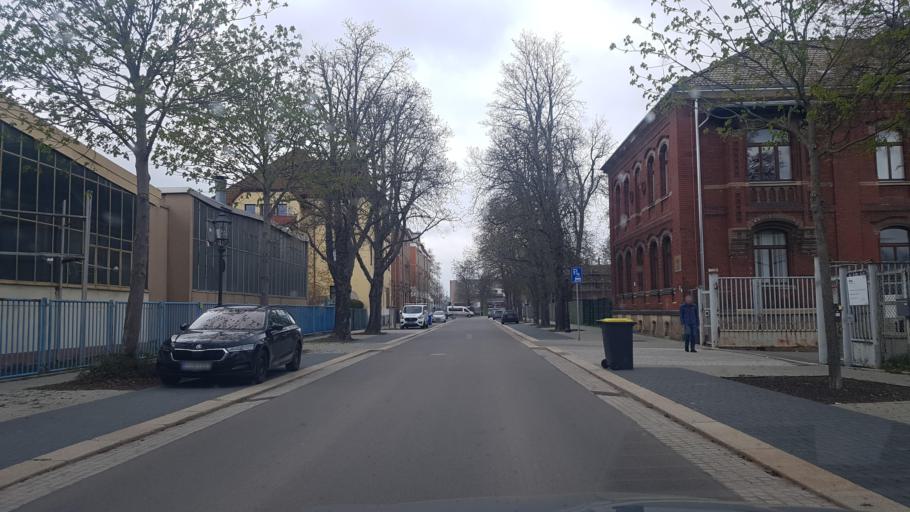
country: DE
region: Saxony
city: Zwickau
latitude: 50.7340
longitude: 12.4840
